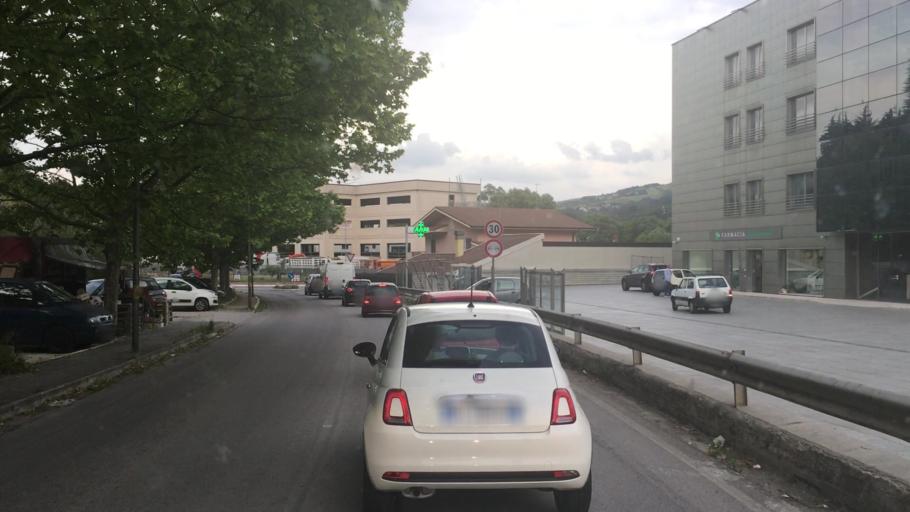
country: IT
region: Basilicate
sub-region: Provincia di Potenza
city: Potenza
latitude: 40.6246
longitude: 15.7917
